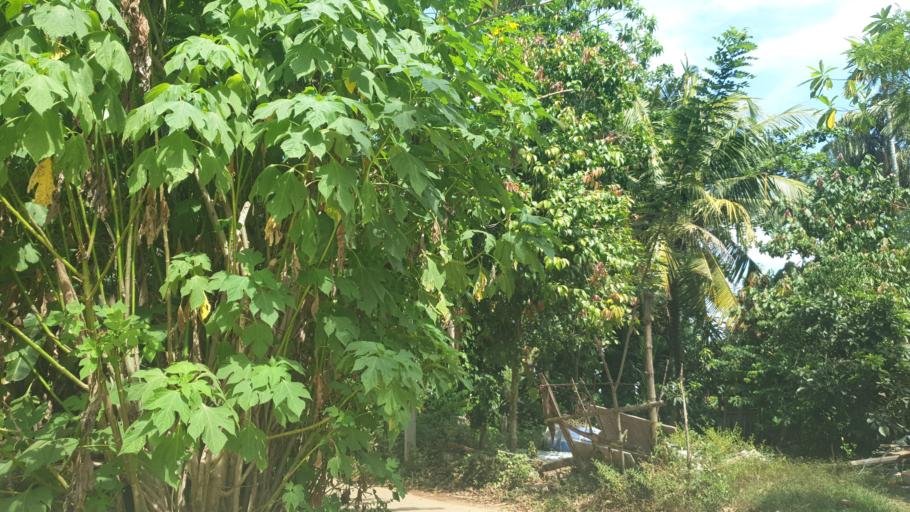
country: LK
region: Southern
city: Tangalla
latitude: 5.9657
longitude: 80.7091
